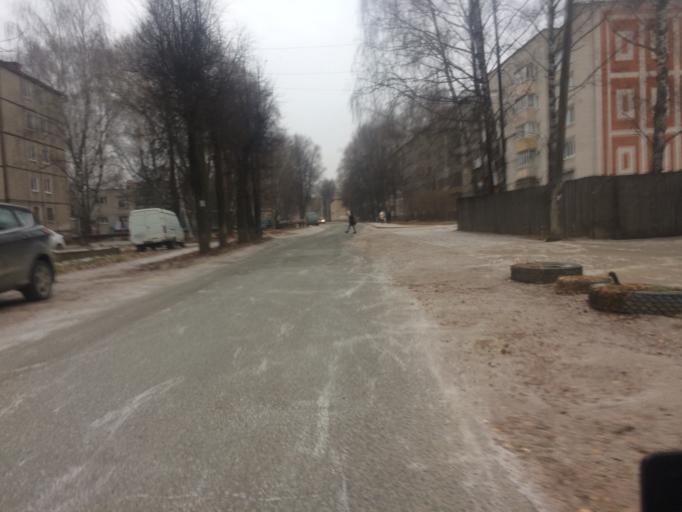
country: RU
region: Mariy-El
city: Yoshkar-Ola
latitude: 56.6428
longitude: 47.8965
